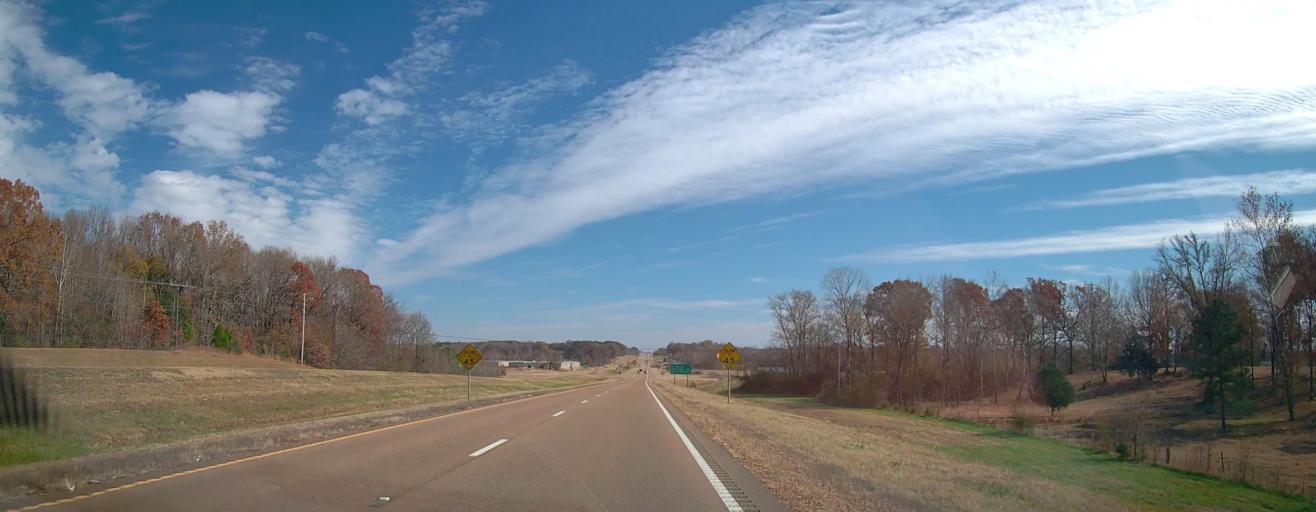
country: US
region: Mississippi
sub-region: Benton County
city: Ashland
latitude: 34.9461
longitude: -89.3017
